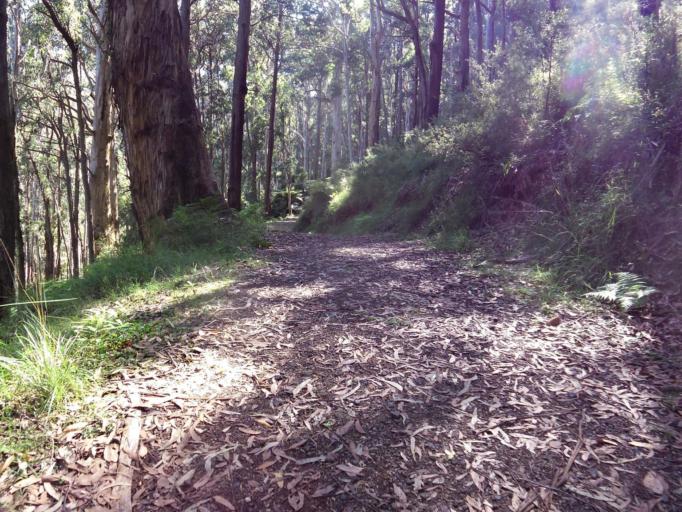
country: AU
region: Victoria
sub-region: Yarra Ranges
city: Olinda
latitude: -37.8459
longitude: 145.3501
